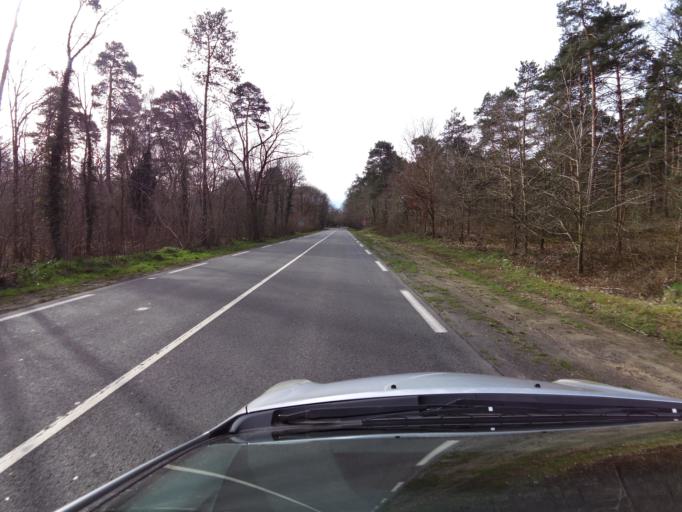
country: FR
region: Picardie
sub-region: Departement de l'Oise
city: Ver-sur-Launette
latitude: 49.1375
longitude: 2.6878
